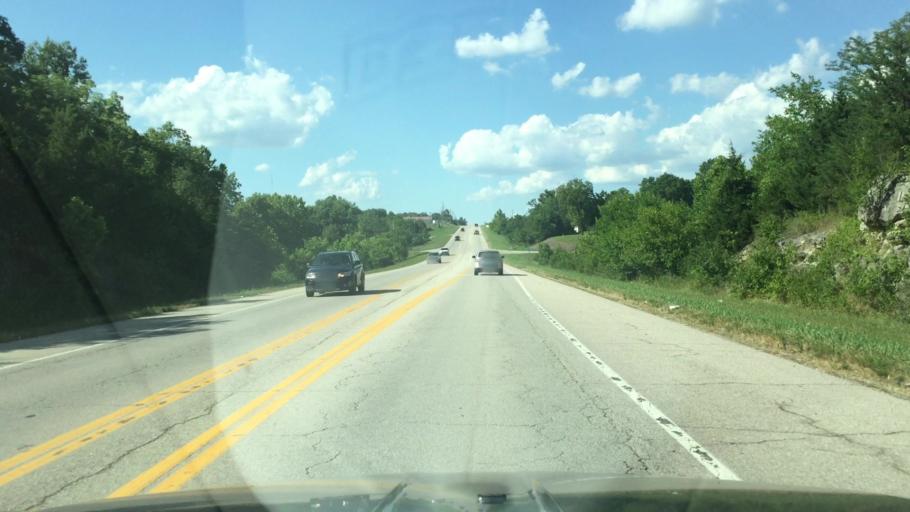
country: US
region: Missouri
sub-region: Miller County
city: Eldon
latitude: 38.3212
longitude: -92.5879
